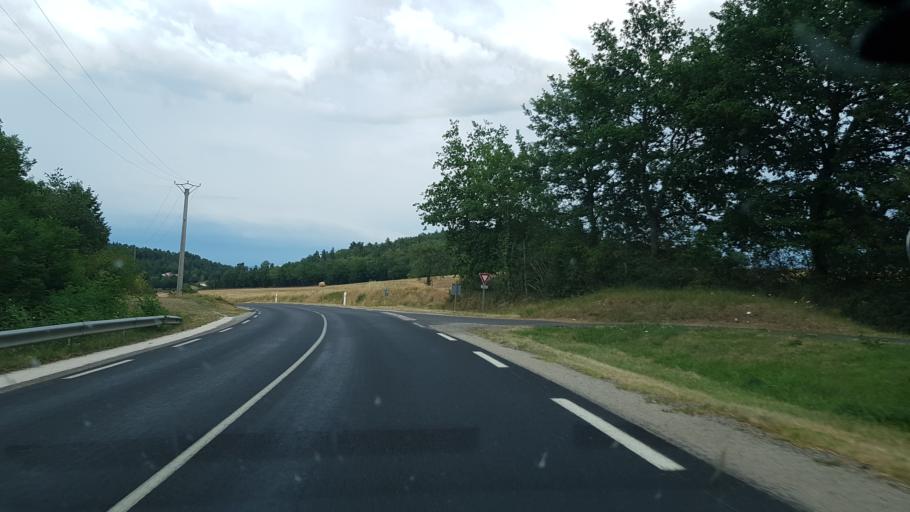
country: FR
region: Auvergne
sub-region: Departement de la Haute-Loire
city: Vieille-Brioude
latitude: 45.2745
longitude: 3.3405
